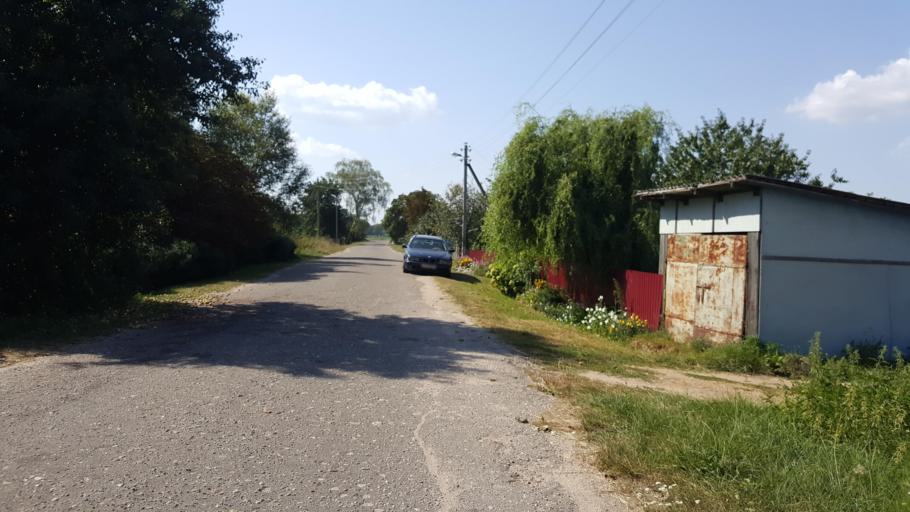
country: PL
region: Podlasie
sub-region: Powiat hajnowski
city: Czeremcha
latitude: 52.4790
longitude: 23.5326
